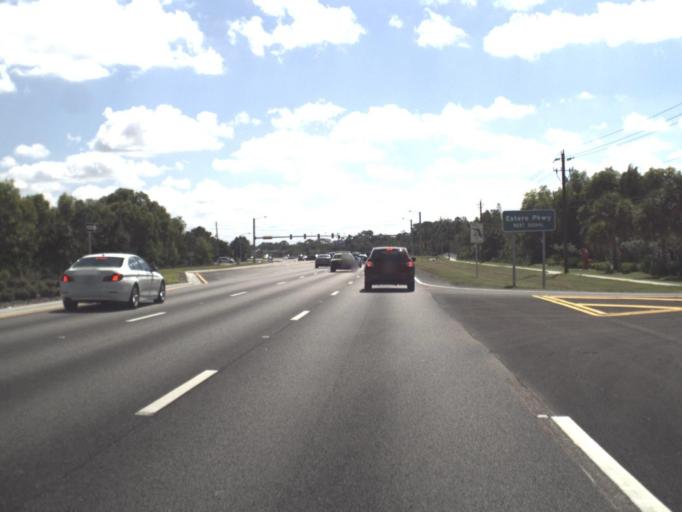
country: US
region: Florida
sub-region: Lee County
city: Estero
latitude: 26.4502
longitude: -81.8196
